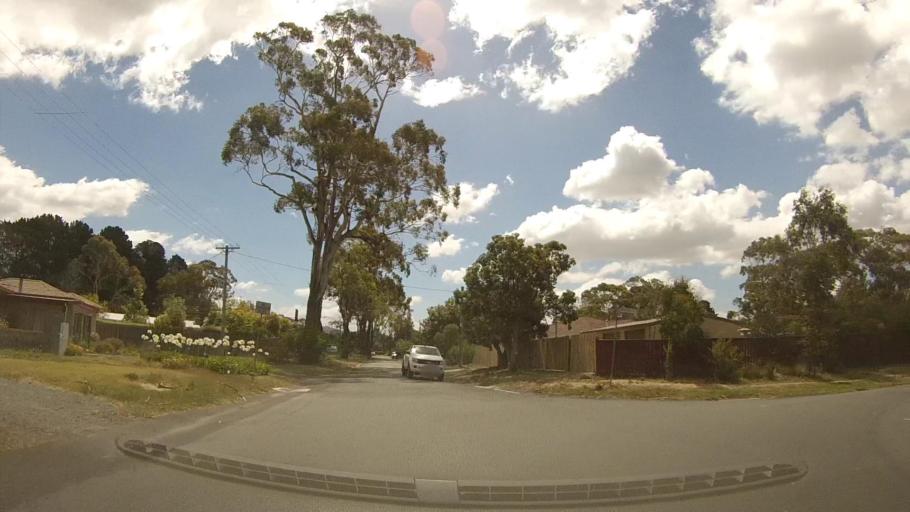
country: AU
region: Tasmania
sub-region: Clarence
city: Seven Mile Beach
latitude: -42.8588
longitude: 147.5010
